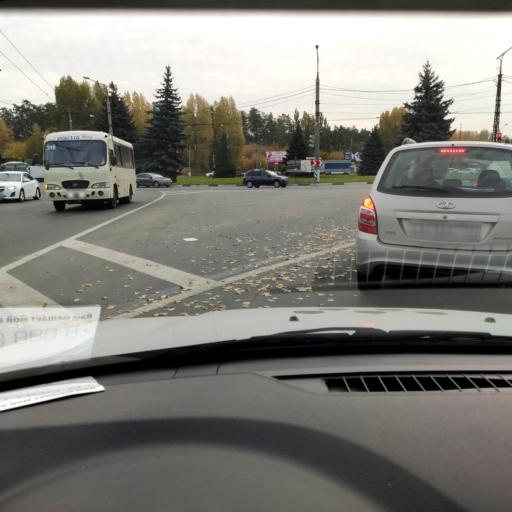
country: RU
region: Samara
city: Zhigulevsk
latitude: 53.5108
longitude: 49.4610
